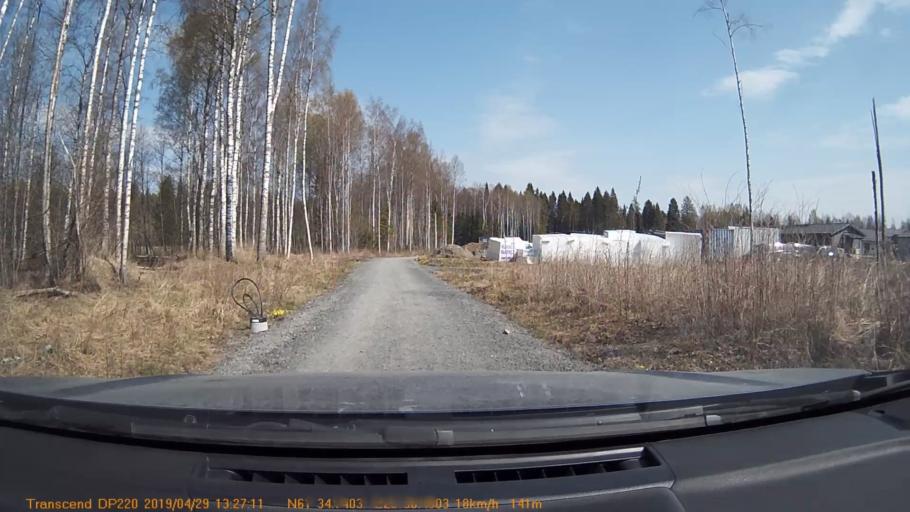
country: FI
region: Pirkanmaa
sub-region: Tampere
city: Yloejaervi
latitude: 61.5790
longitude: 23.5080
